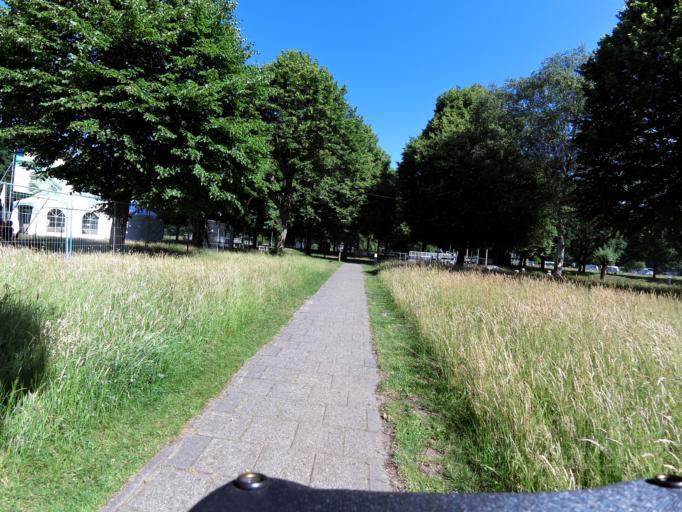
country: NL
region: Overijssel
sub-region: Gemeente Dalfsen
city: Dalfsen
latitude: 52.5208
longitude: 6.3362
